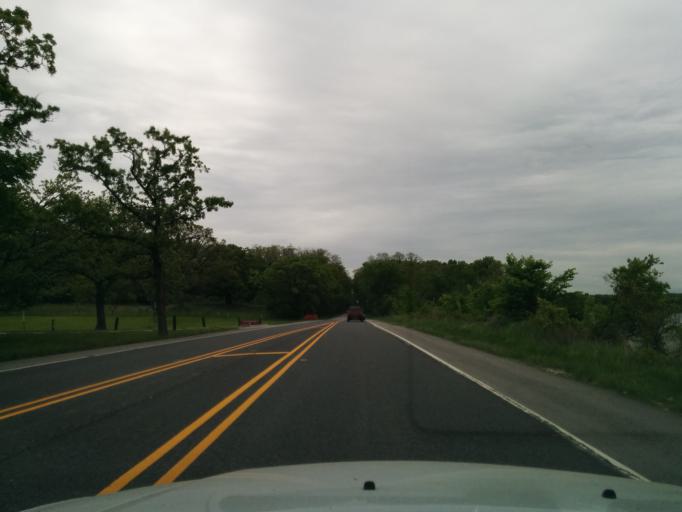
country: US
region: Illinois
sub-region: Cook County
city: Willow Springs
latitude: 41.7158
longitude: -87.8758
